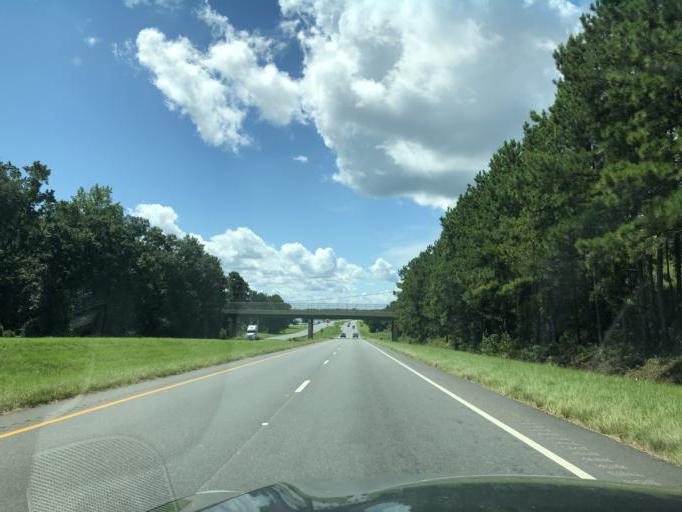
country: US
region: Alabama
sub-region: Barbour County
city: Eufaula
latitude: 31.9919
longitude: -85.1151
